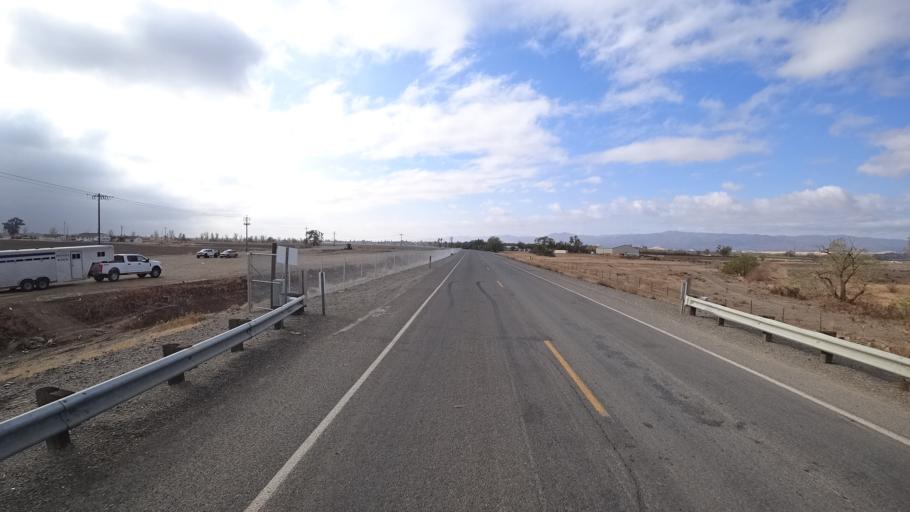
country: US
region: California
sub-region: Yolo County
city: Esparto
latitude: 38.7116
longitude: -122.0117
